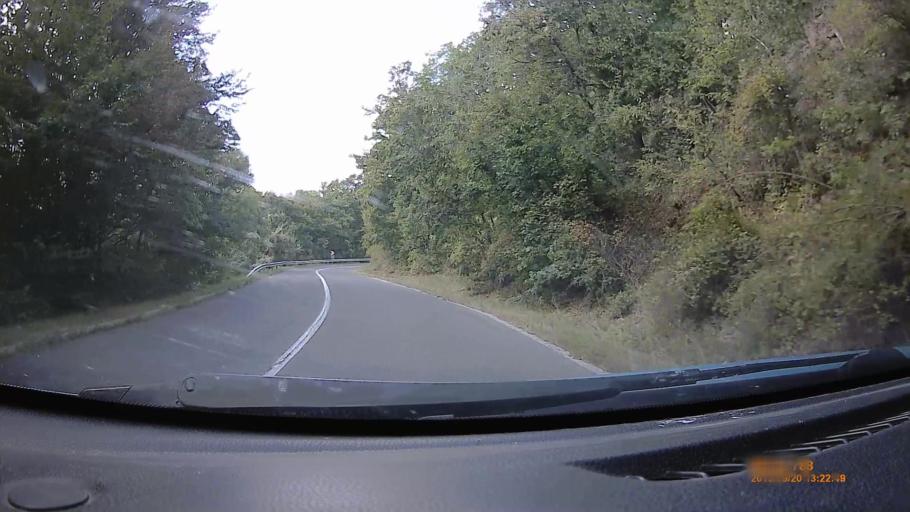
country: HU
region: Heves
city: Felsotarkany
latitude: 48.0297
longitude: 20.4797
